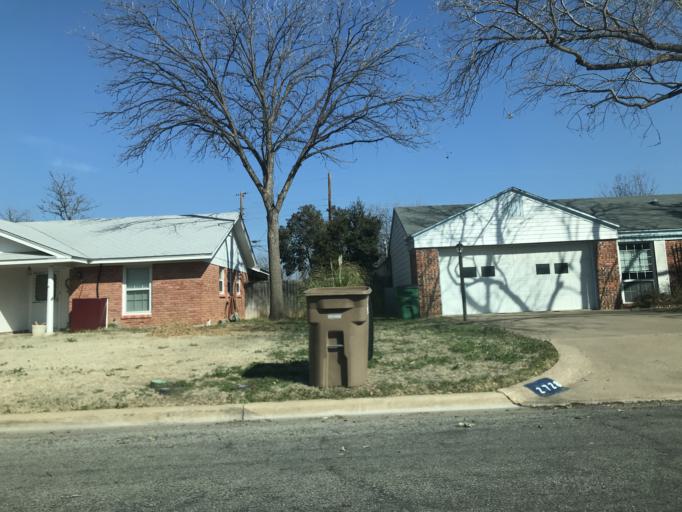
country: US
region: Texas
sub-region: Tom Green County
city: San Angelo
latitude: 31.4350
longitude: -100.4718
